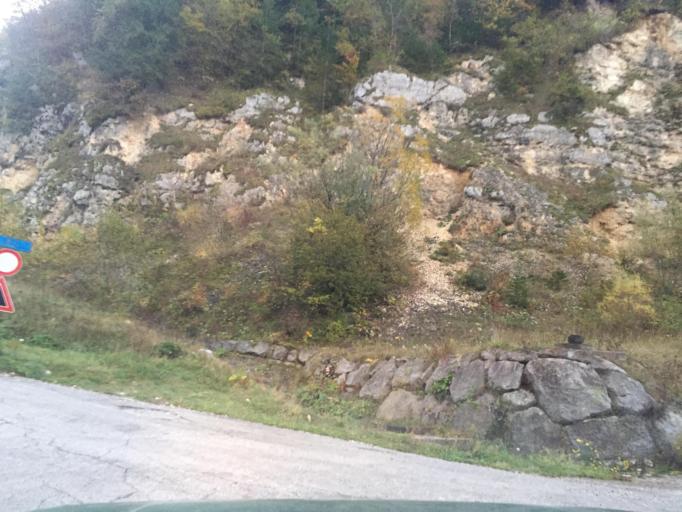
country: IT
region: Friuli Venezia Giulia
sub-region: Provincia di Pordenone
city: Andreis
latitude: 46.1949
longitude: 12.6430
